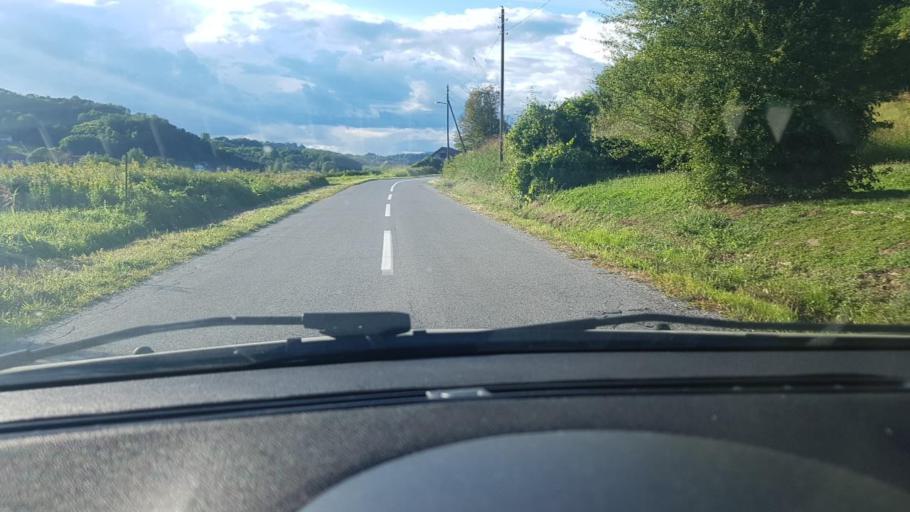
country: HR
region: Krapinsko-Zagorska
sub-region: Grad Krapina
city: Krapina
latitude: 46.1038
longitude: 15.8186
